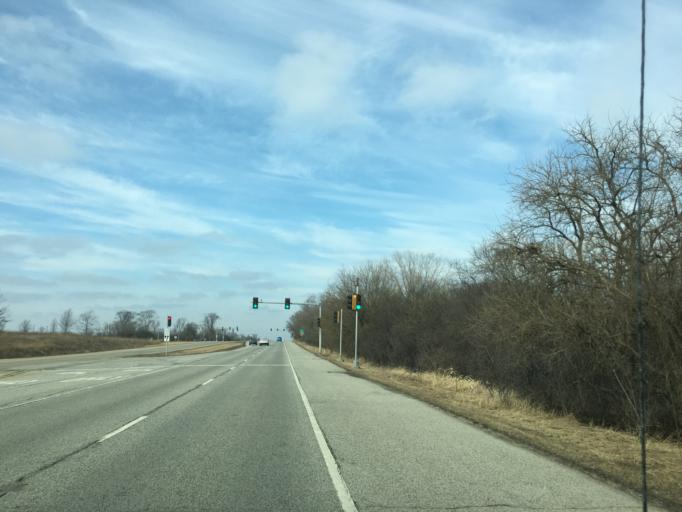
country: US
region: Illinois
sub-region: Kane County
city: East Dundee
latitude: 42.0811
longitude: -88.2194
